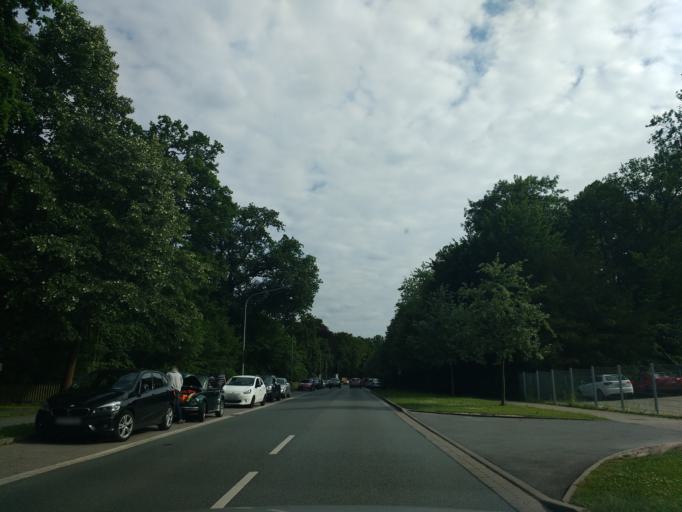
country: DE
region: North Rhine-Westphalia
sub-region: Regierungsbezirk Detmold
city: Lemgo
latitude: 52.0373
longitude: 8.9026
